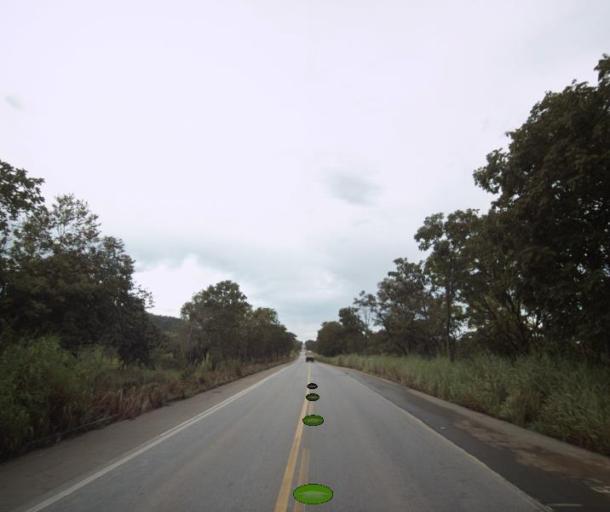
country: BR
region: Goias
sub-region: Porangatu
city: Porangatu
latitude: -13.6279
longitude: -49.0427
